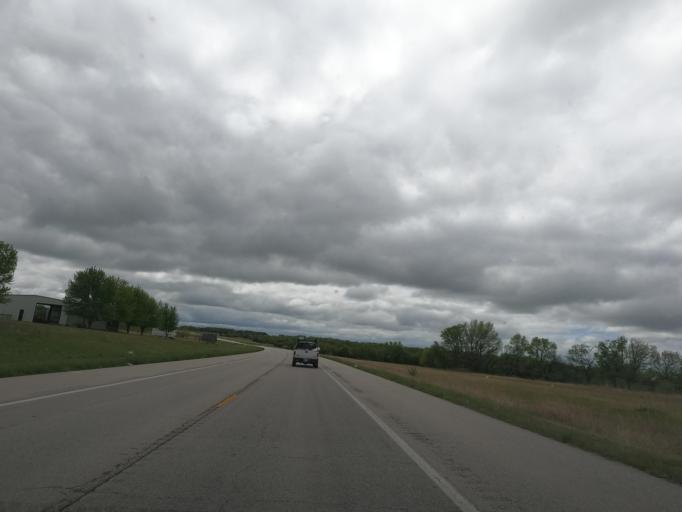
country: US
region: Kansas
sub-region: Wilson County
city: Fredonia
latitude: 37.5213
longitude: -95.8009
